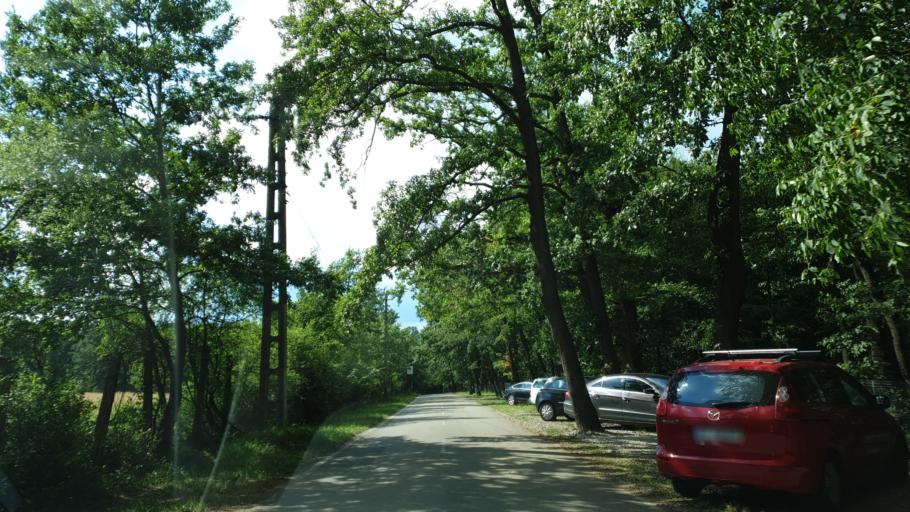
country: RO
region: Hunedoara
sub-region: Comuna Turdas
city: Pricaz
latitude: 45.8317
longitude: 23.1651
